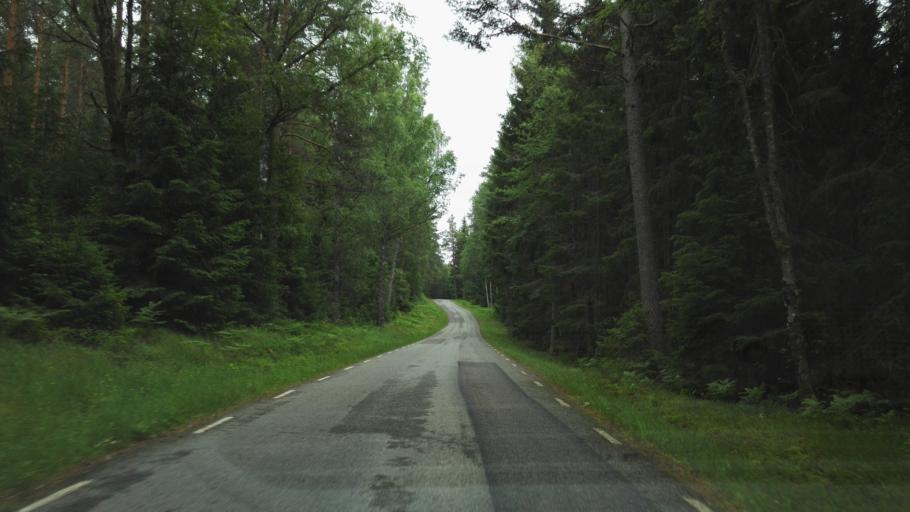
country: SE
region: Kronoberg
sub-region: Vaxjo Kommun
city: Rottne
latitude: 57.1536
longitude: 14.8056
